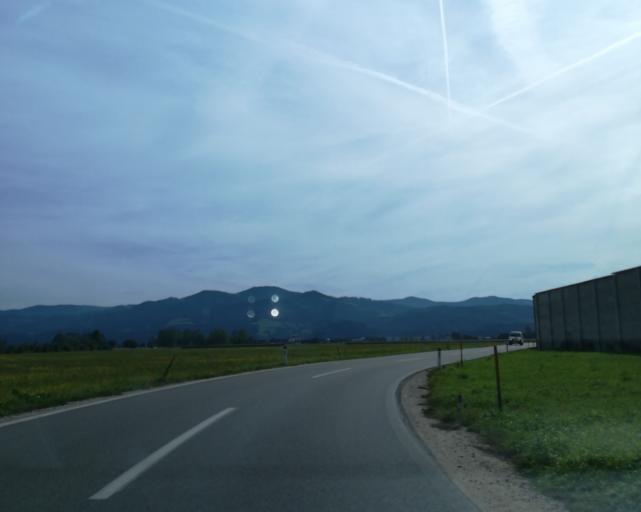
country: AT
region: Styria
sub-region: Politischer Bezirk Murtal
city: Flatschach
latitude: 47.2067
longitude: 14.7588
